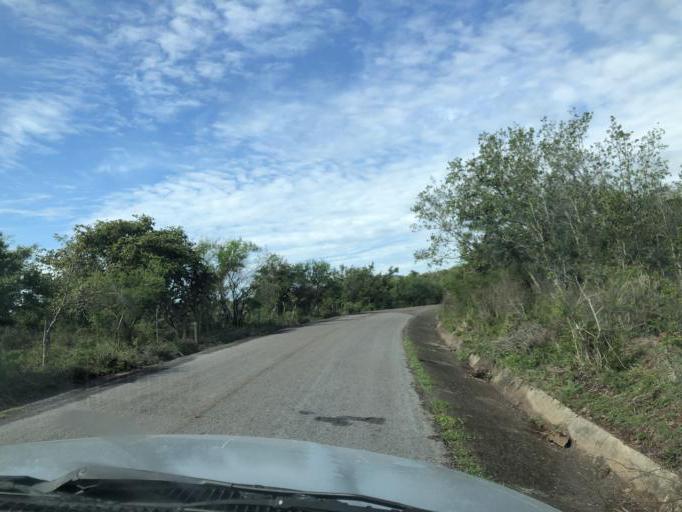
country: MX
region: Veracruz
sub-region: Alto Lucero de Gutierrez Barrios
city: Palma Sola
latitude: 19.7941
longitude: -96.5484
